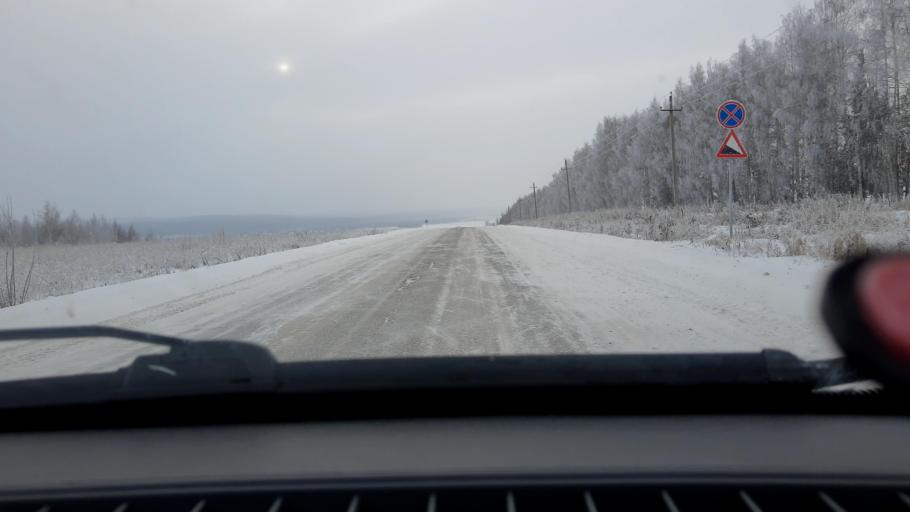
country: RU
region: Bashkortostan
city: Iglino
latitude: 54.6577
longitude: 56.4249
